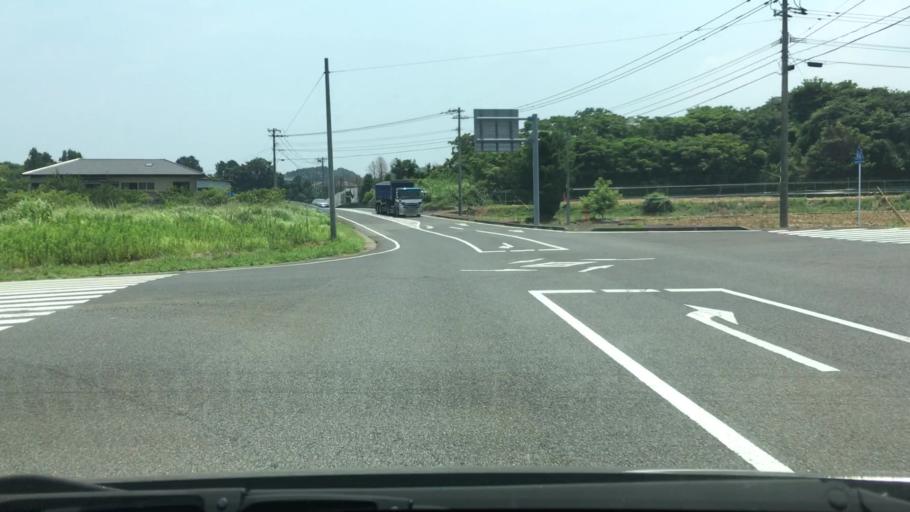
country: JP
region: Nagasaki
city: Sasebo
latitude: 33.0672
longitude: 129.6830
